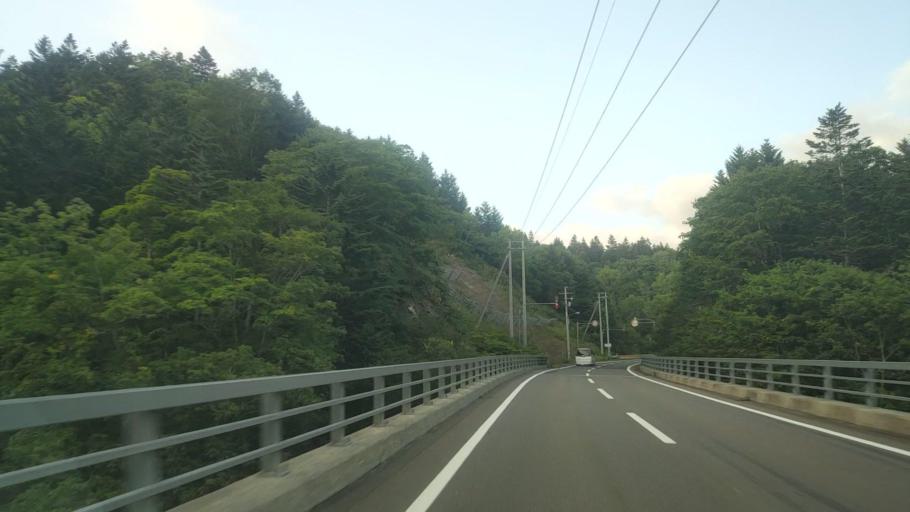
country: JP
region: Hokkaido
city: Bibai
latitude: 43.2740
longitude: 142.0398
